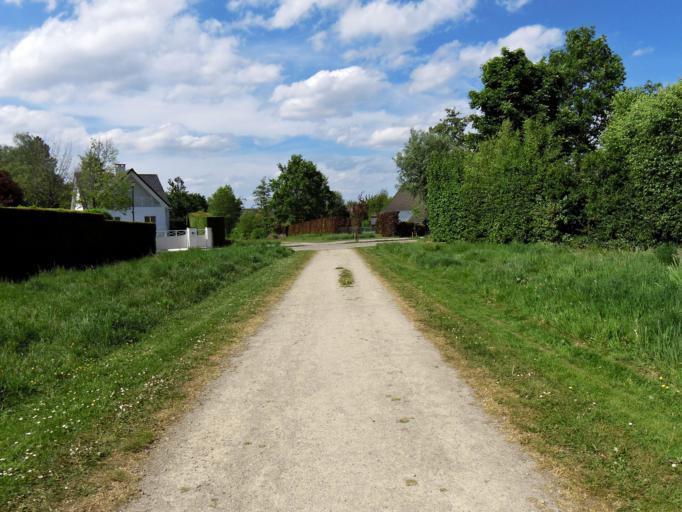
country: BE
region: Flanders
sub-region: Provincie Vlaams-Brabant
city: Wezembeek-Oppem
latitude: 50.8583
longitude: 4.5018
